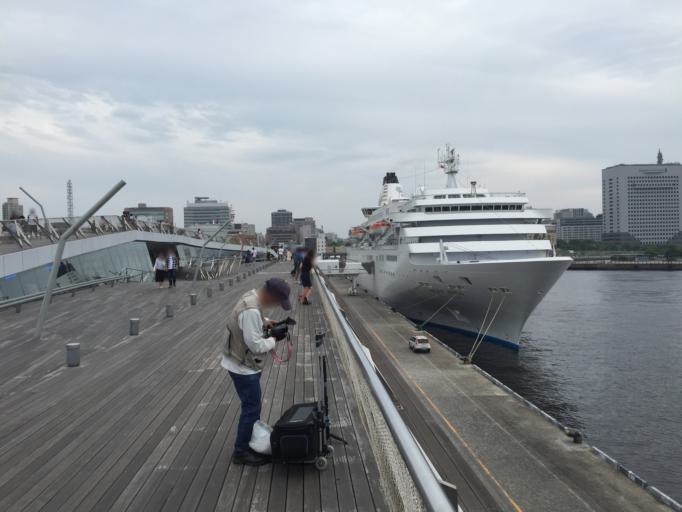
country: JP
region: Kanagawa
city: Yokohama
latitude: 35.4528
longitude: 139.6482
